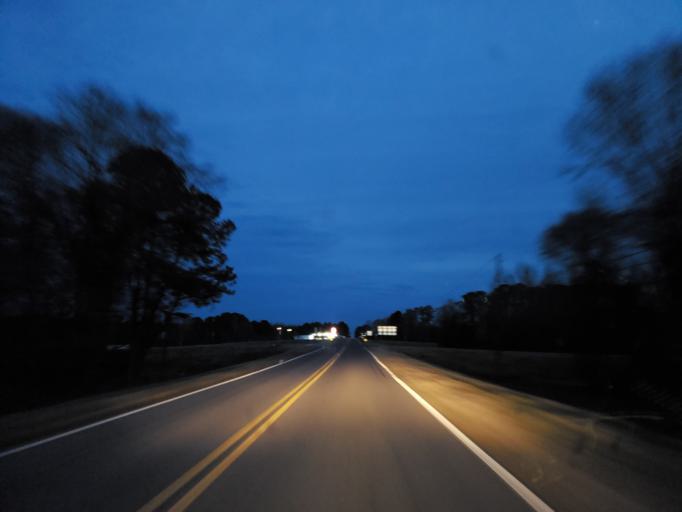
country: US
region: Alabama
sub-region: Greene County
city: Eutaw
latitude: 32.8699
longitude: -87.9265
